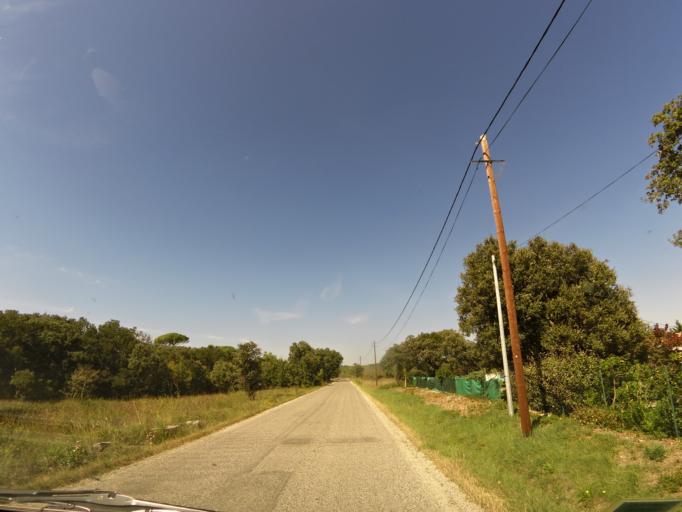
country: FR
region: Languedoc-Roussillon
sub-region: Departement du Gard
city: Uchaud
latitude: 43.7645
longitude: 4.2536
